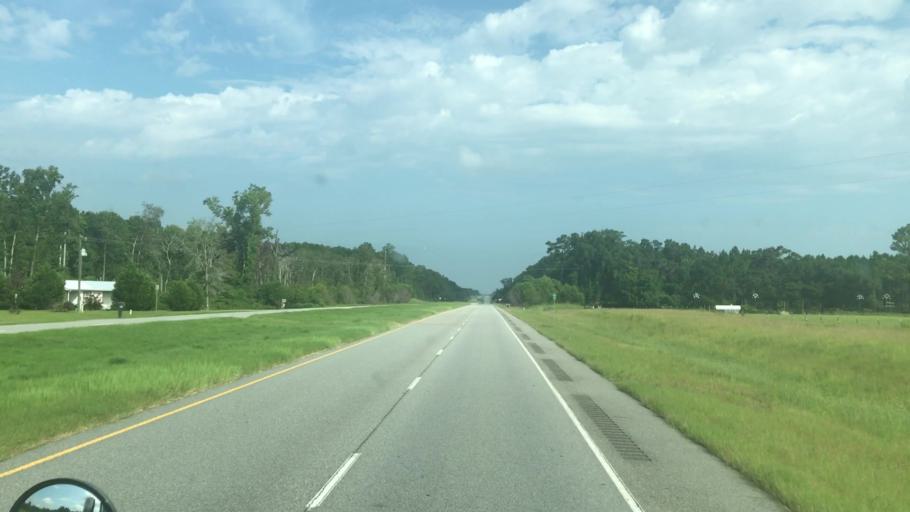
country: US
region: Georgia
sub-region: Early County
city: Blakely
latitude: 31.2931
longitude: -84.8514
